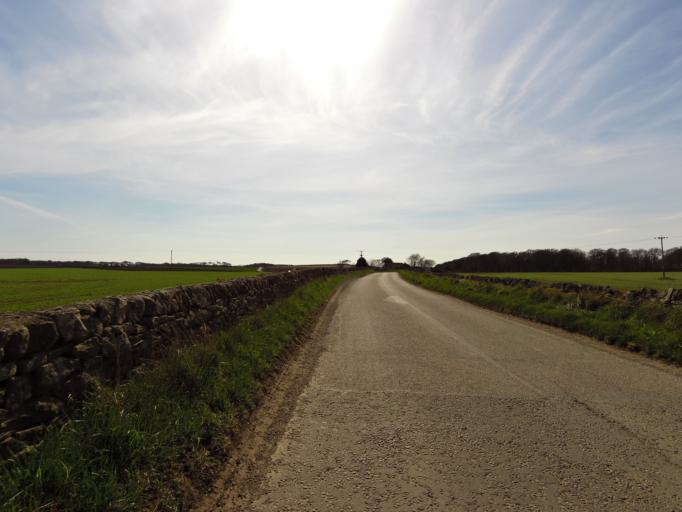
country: GB
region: Scotland
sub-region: Angus
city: Arbroath
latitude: 56.5947
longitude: -2.5521
